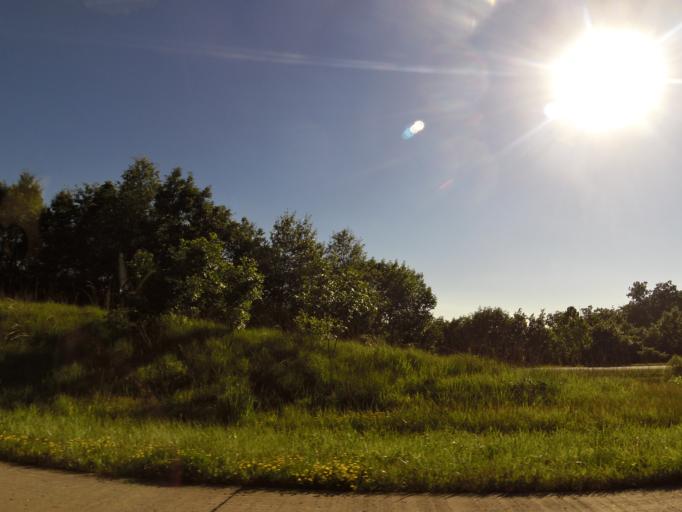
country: US
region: Missouri
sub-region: Pike County
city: Bowling Green
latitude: 39.4124
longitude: -91.2493
